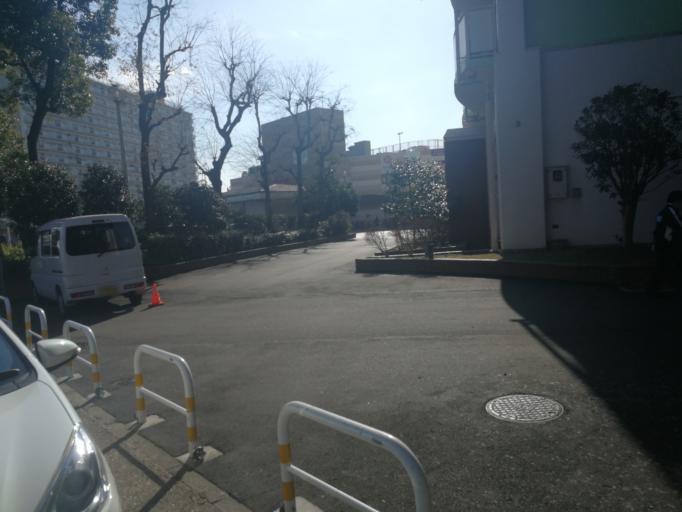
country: JP
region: Kyoto
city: Uji
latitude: 34.9192
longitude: 135.7774
